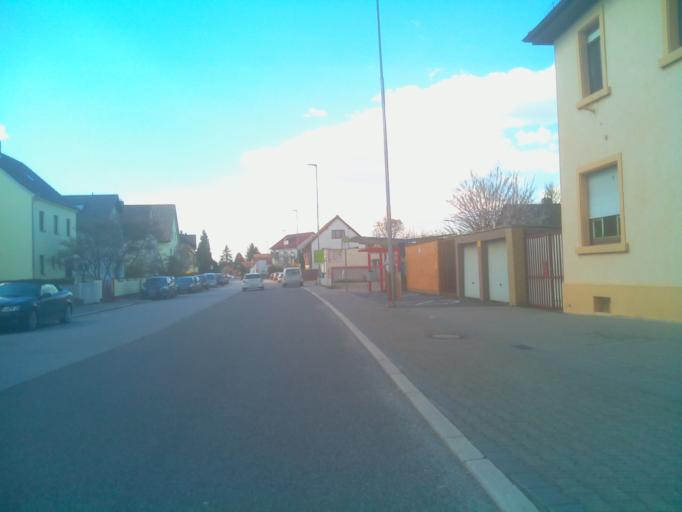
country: DE
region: Baden-Wuerttemberg
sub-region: Karlsruhe Region
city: Ilvesheim
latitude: 49.4806
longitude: 8.5565
